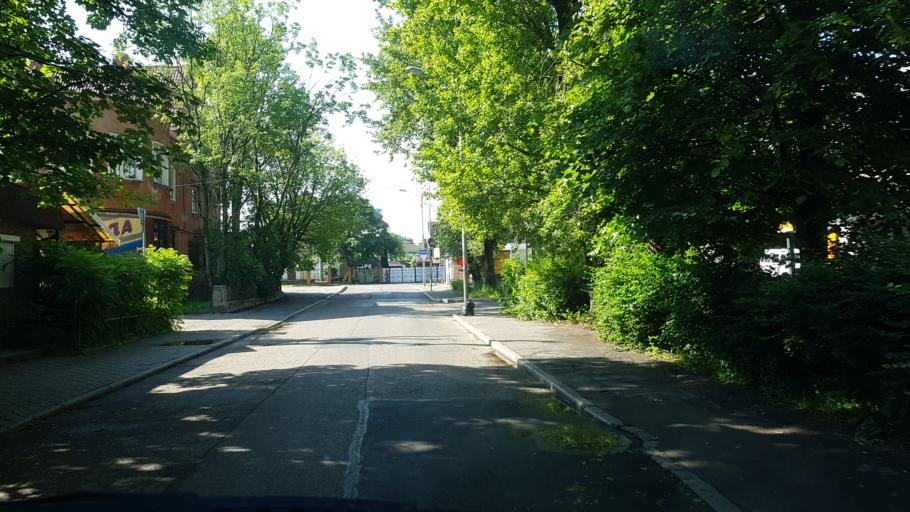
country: RU
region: Kaliningrad
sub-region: Gorod Kaliningrad
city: Kaliningrad
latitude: 54.7151
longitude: 20.4568
